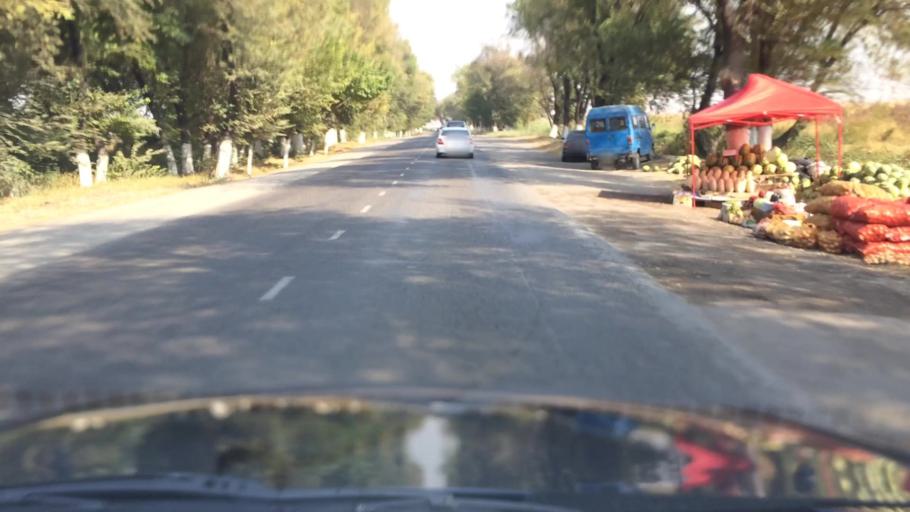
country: KG
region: Chuy
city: Lebedinovka
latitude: 42.8961
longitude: 74.6829
